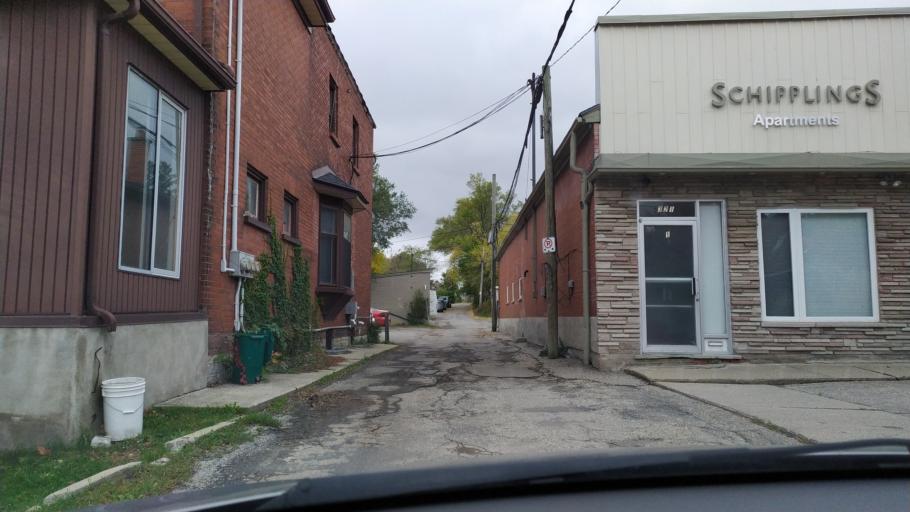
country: CA
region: Ontario
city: Waterloo
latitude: 43.4559
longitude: -80.4969
